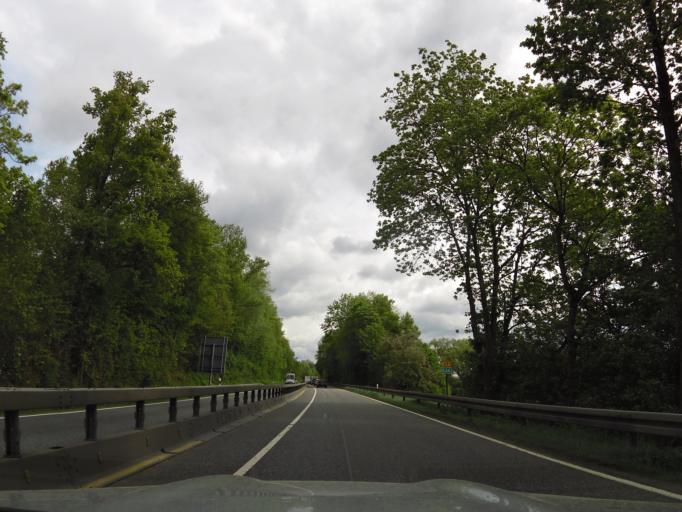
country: DE
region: Hesse
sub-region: Regierungsbezirk Giessen
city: Lohnberg
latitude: 50.5207
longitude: 8.2746
